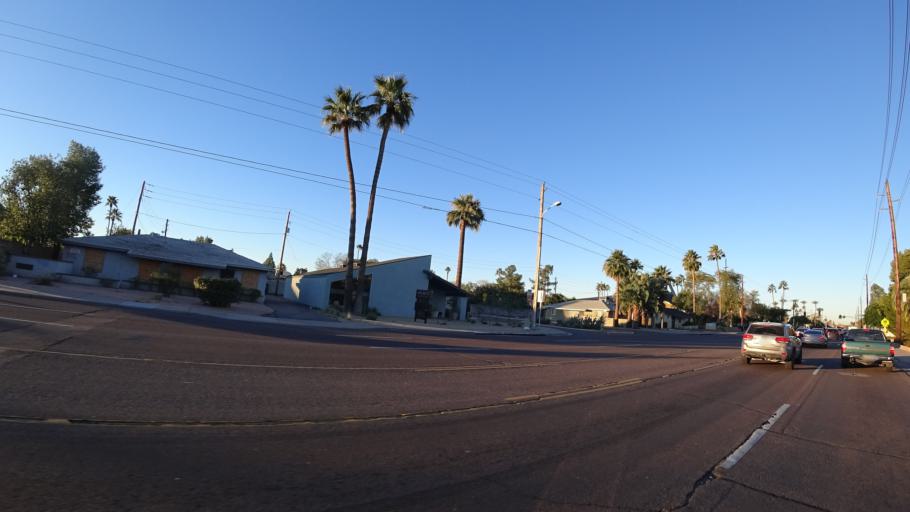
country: US
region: Arizona
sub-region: Maricopa County
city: Paradise Valley
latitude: 33.4801
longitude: -111.9707
